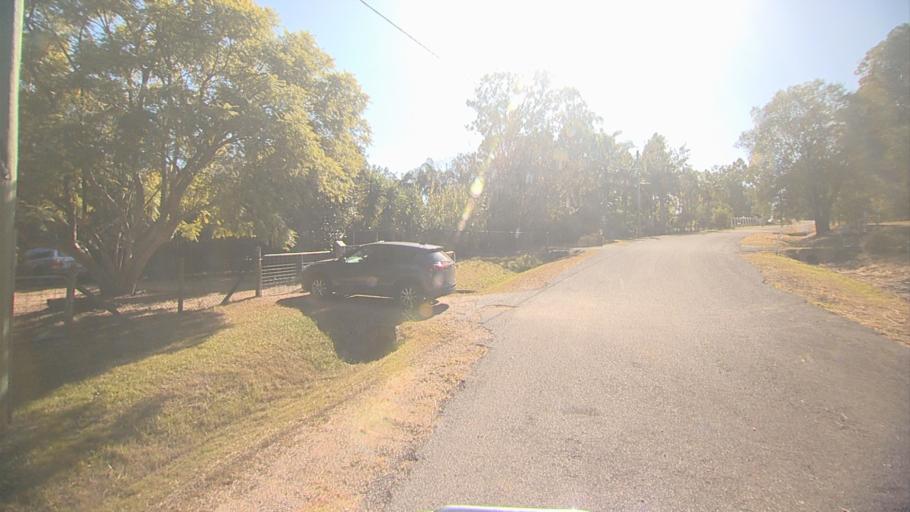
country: AU
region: Queensland
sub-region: Logan
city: Cedar Vale
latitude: -27.8579
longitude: 152.9863
